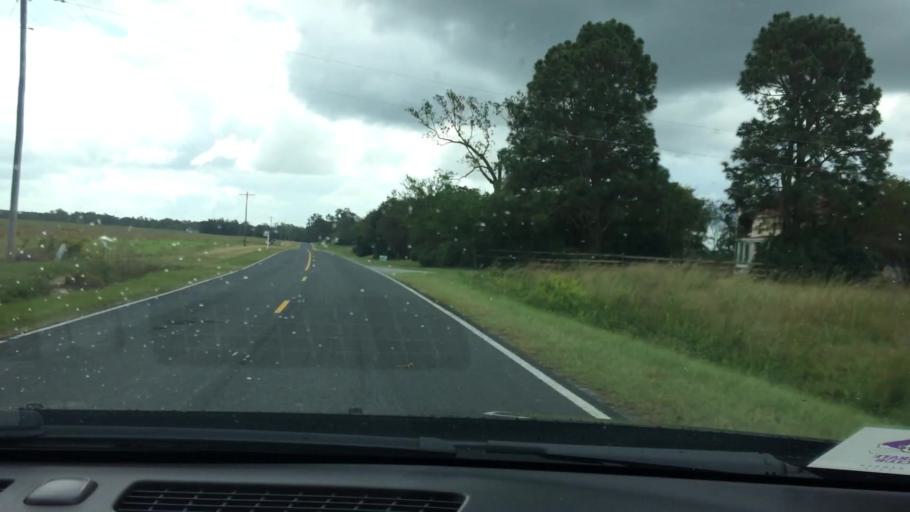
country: US
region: North Carolina
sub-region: Greene County
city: Maury
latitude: 35.5095
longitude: -77.5256
